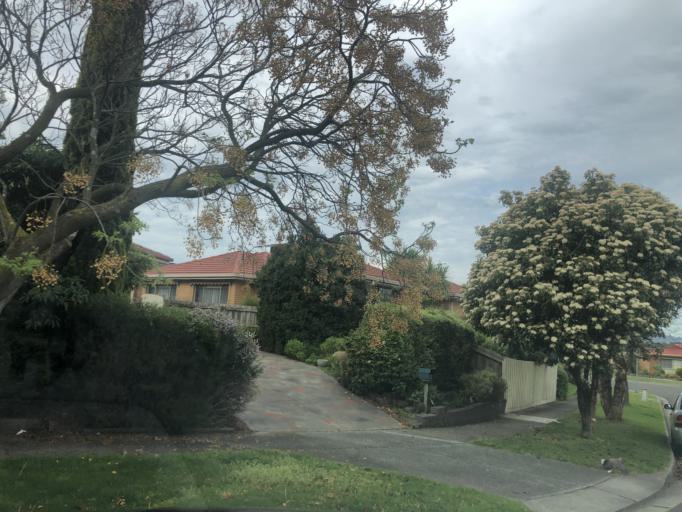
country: AU
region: Victoria
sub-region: Casey
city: Hallam
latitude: -38.0115
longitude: 145.2766
